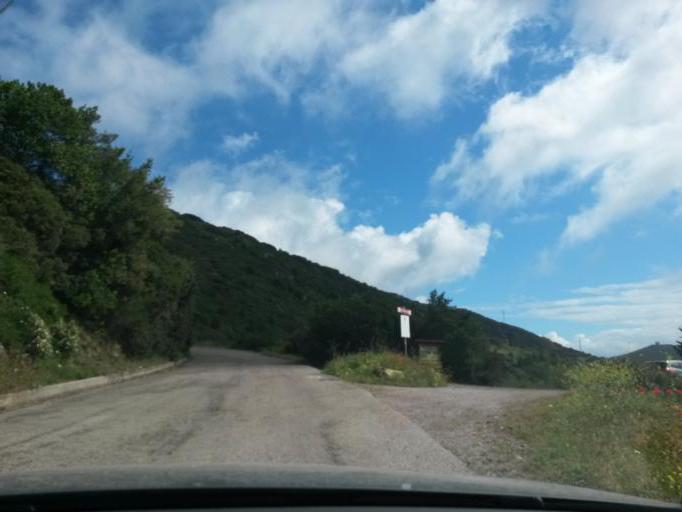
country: IT
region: Tuscany
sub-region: Provincia di Livorno
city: Rio nell'Elba
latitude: 42.8243
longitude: 10.4041
